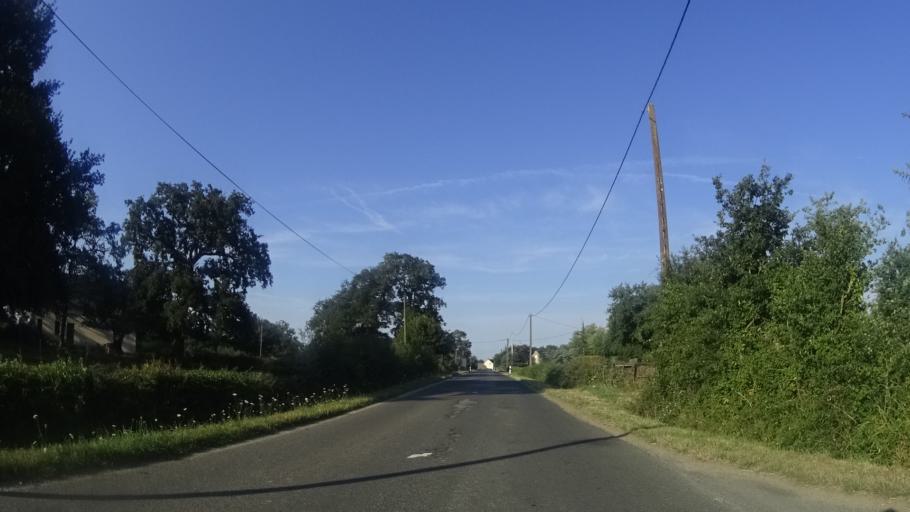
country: FR
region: Pays de la Loire
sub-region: Departement de la Loire-Atlantique
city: Mouzeil
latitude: 47.4891
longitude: -1.3516
